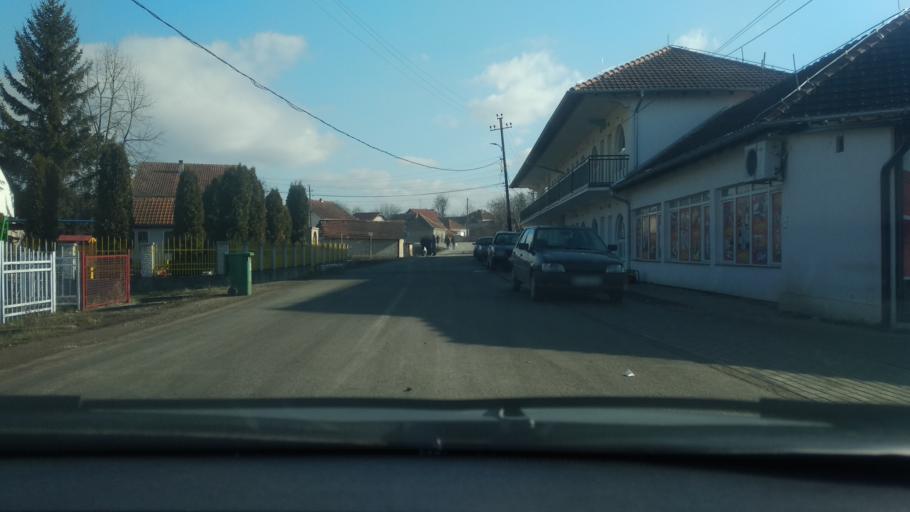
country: XK
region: Pristina
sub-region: Lipjan
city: Lipljan
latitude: 42.5463
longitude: 21.1800
